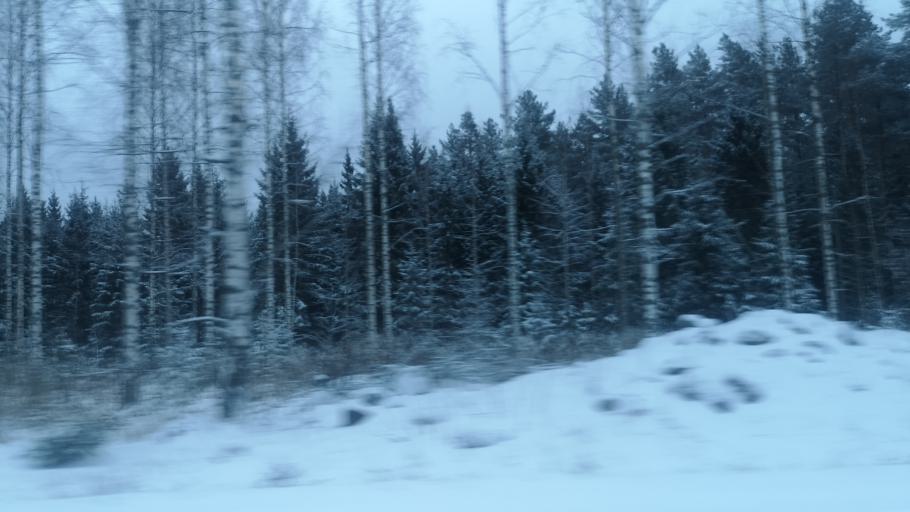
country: FI
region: Southern Savonia
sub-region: Savonlinna
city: Savonlinna
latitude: 62.0064
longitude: 28.7366
